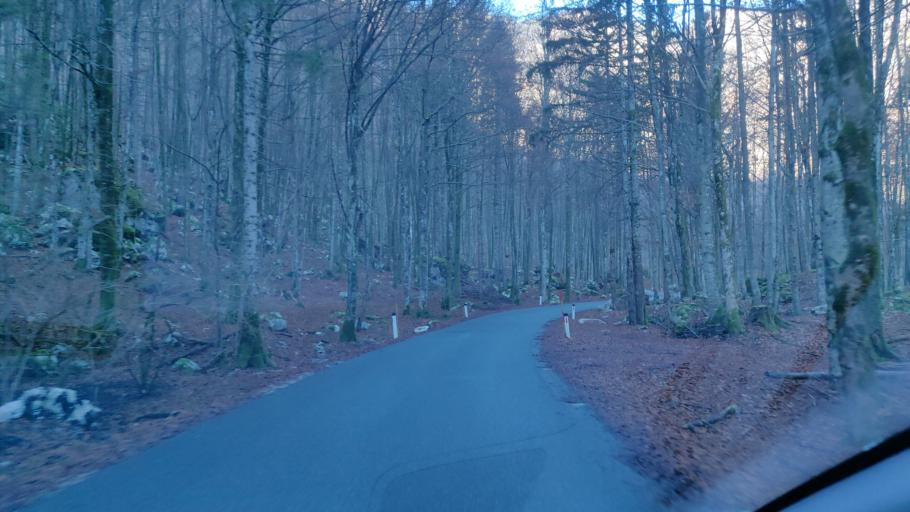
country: SI
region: Tolmin
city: Tolmin
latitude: 46.2772
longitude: 13.8135
